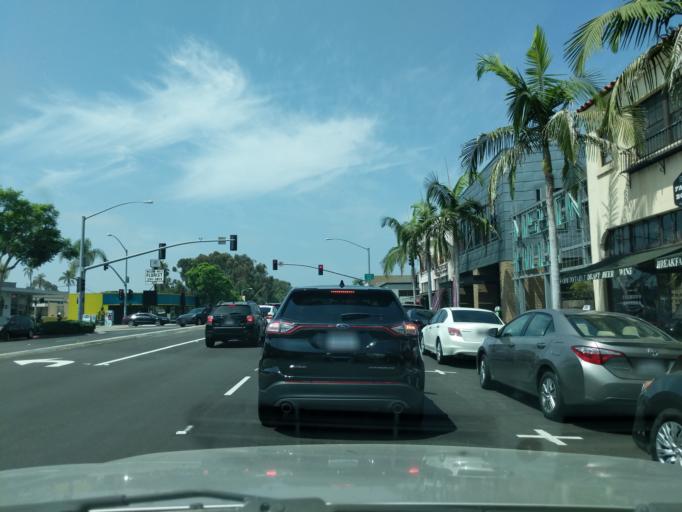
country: US
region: California
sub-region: San Diego County
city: San Diego
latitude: 32.7499
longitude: -117.1708
